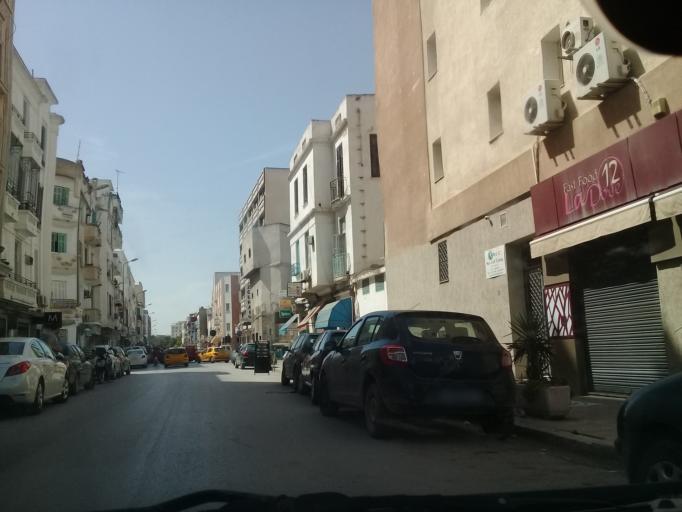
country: TN
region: Tunis
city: Tunis
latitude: 36.8107
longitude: 10.1778
